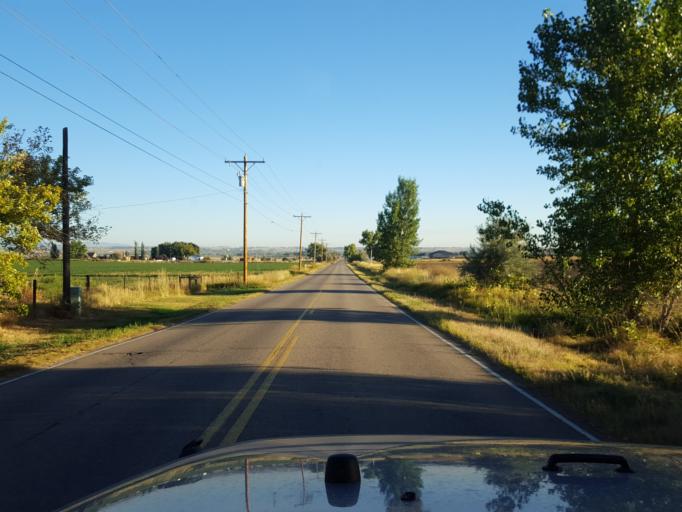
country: US
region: Colorado
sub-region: Weld County
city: Firestone
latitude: 40.1097
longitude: -104.9988
